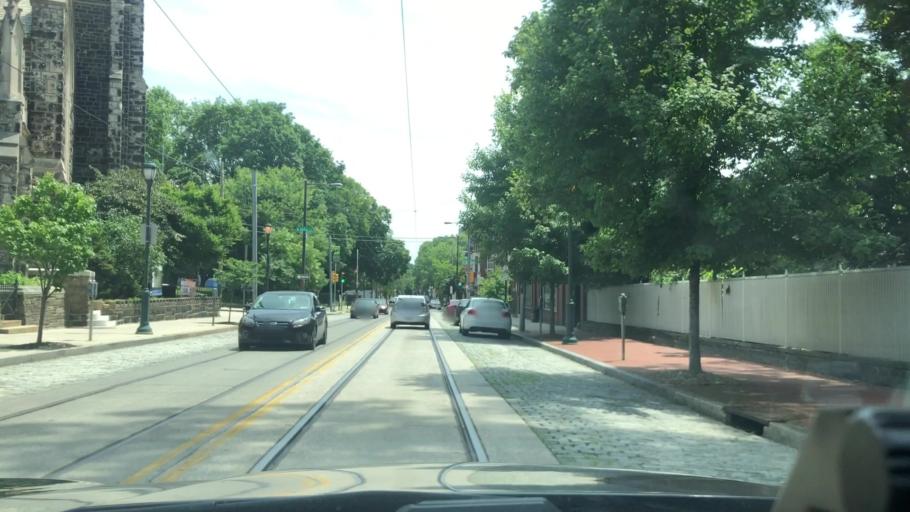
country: US
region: Pennsylvania
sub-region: Montgomery County
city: Wyndmoor
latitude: 40.0399
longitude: -75.1783
